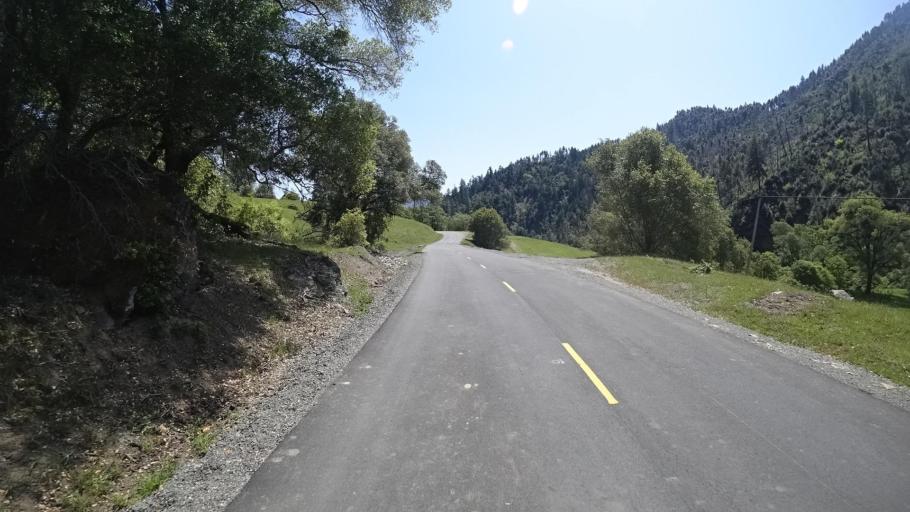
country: US
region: California
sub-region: Humboldt County
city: Redway
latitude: 40.2287
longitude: -123.6118
